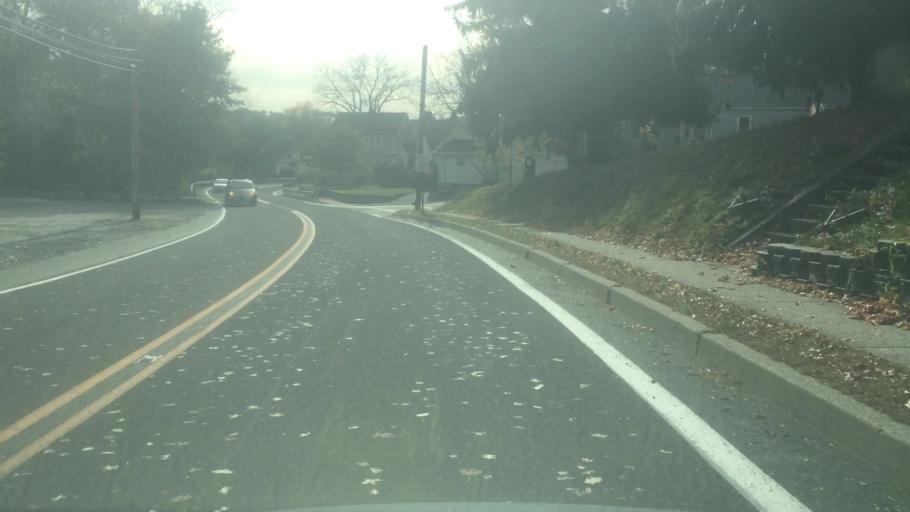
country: US
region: New Jersey
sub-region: Morris County
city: Butler
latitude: 41.0098
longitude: -74.3348
